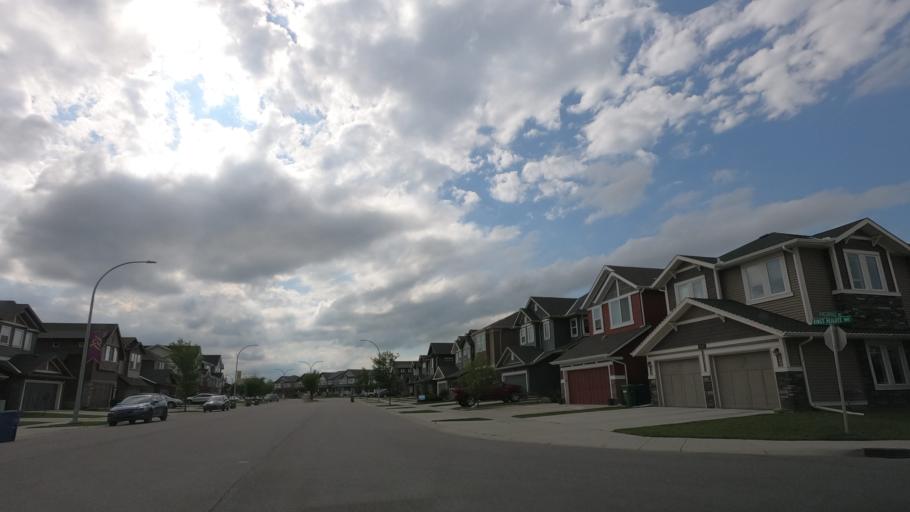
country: CA
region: Alberta
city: Airdrie
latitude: 51.2592
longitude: -113.9866
